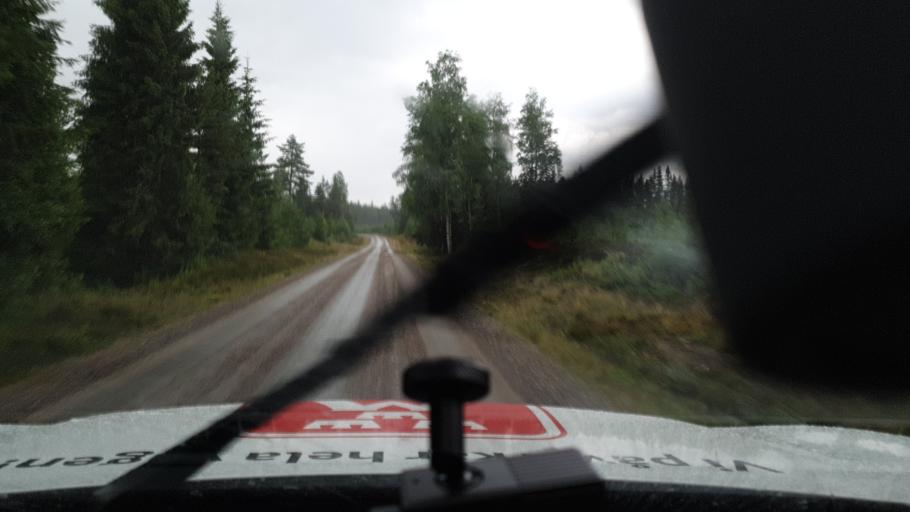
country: SE
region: Vaermland
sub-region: Torsby Kommun
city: Torsby
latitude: 60.3668
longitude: 13.0682
